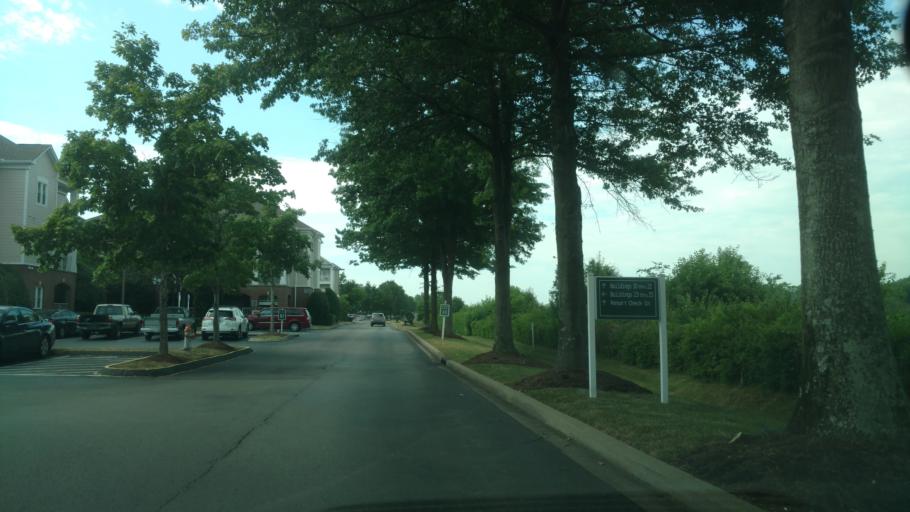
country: US
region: Tennessee
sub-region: Davidson County
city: Lakewood
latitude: 36.2183
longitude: -86.7036
